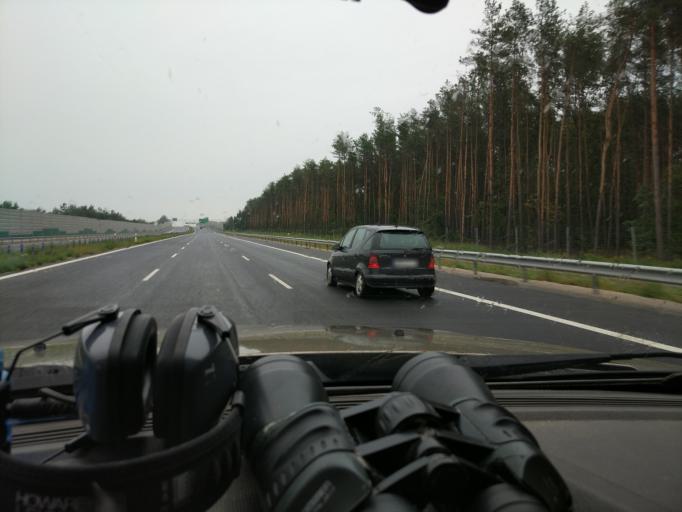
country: PL
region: Masovian Voivodeship
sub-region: Powiat wolominski
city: Radzymin
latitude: 52.3860
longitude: 21.1936
